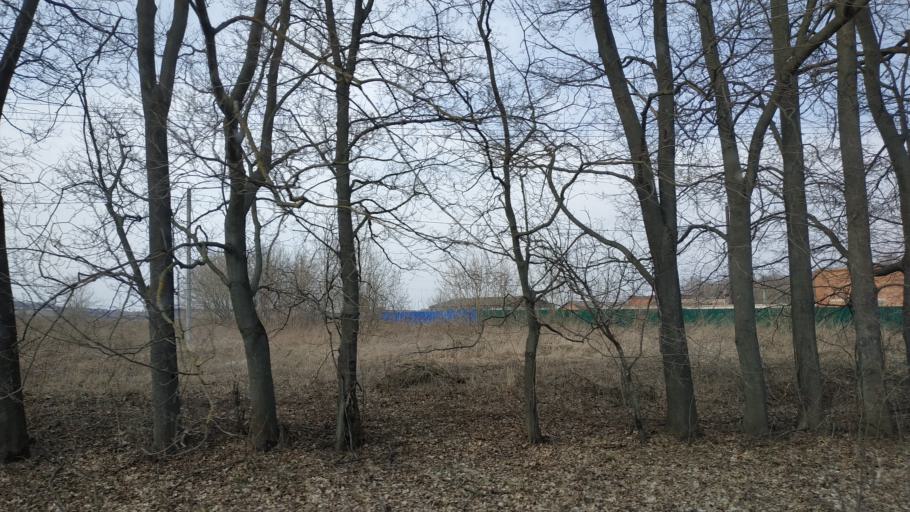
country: RU
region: Moskovskaya
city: Malyshevo
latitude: 55.3984
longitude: 38.3585
